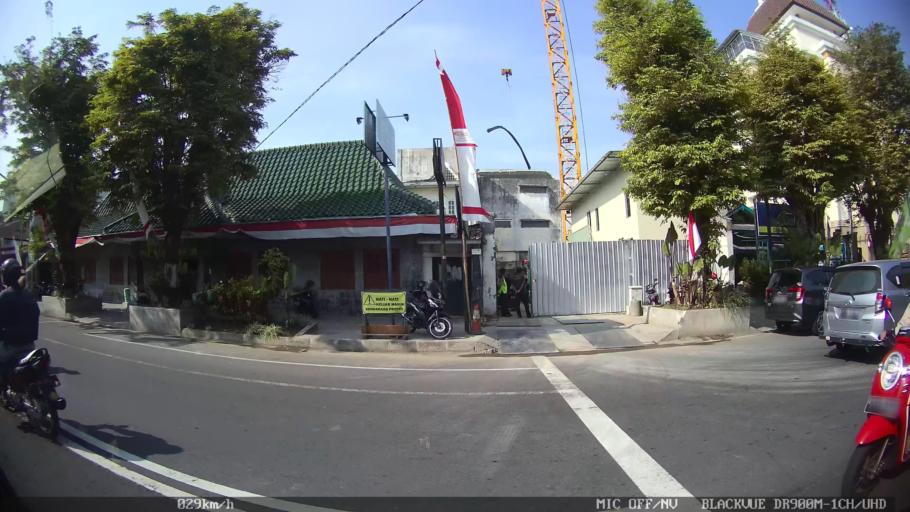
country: ID
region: Daerah Istimewa Yogyakarta
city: Yogyakarta
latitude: -7.8012
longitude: 110.3577
